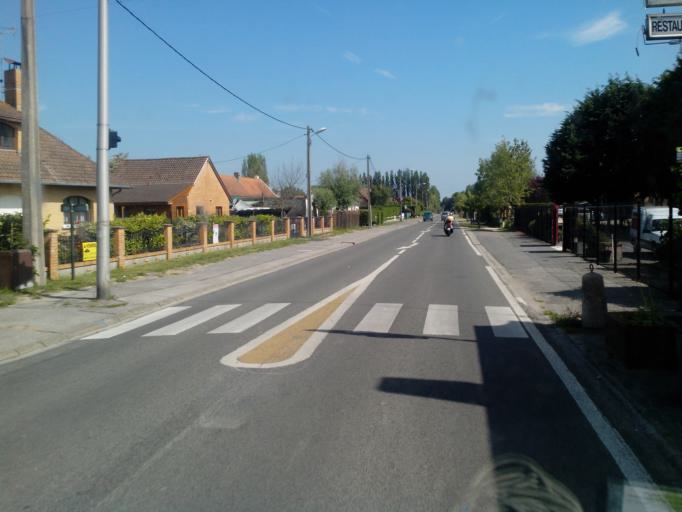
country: FR
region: Nord-Pas-de-Calais
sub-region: Departement du Pas-de-Calais
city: Groffliers
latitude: 50.3880
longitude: 1.6099
